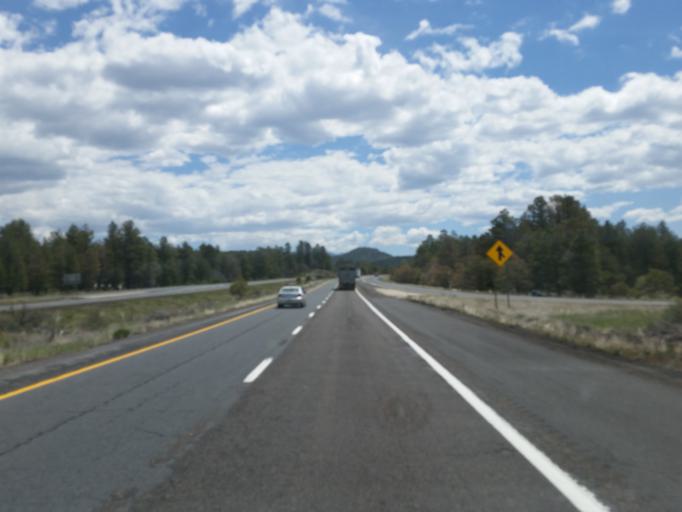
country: US
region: Arizona
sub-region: Coconino County
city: Parks
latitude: 35.2558
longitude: -111.9372
